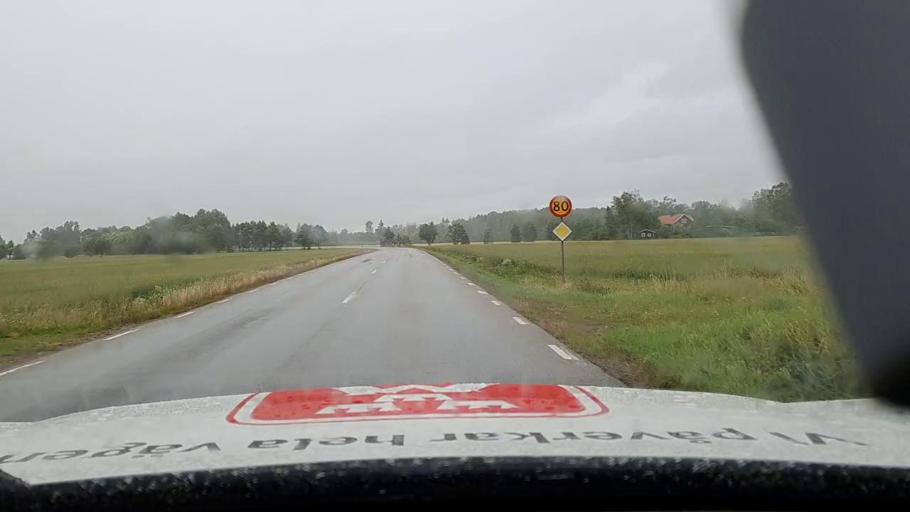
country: SE
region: Vaestra Goetaland
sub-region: Toreboda Kommun
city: Toereboda
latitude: 58.6962
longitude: 14.1327
